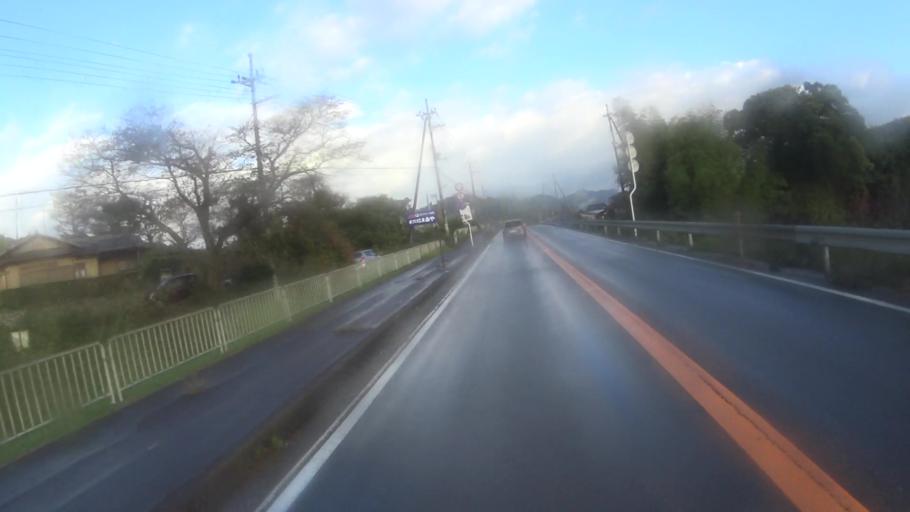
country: JP
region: Kyoto
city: Ayabe
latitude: 35.2448
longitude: 135.2165
